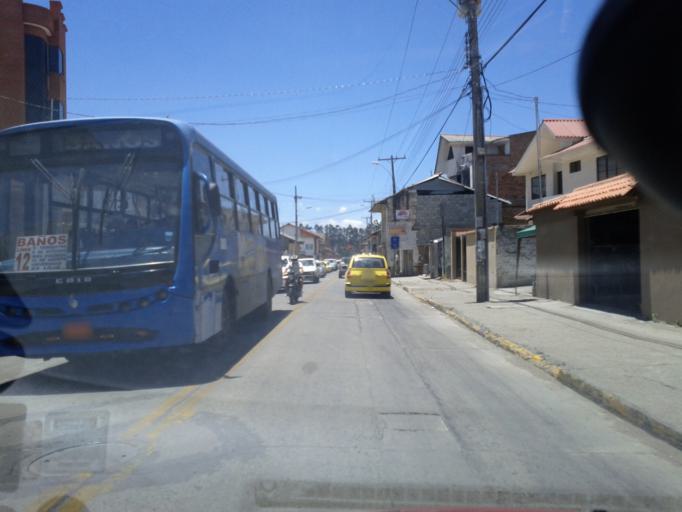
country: EC
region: Azuay
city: Cuenca
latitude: -2.9116
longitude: -79.0295
